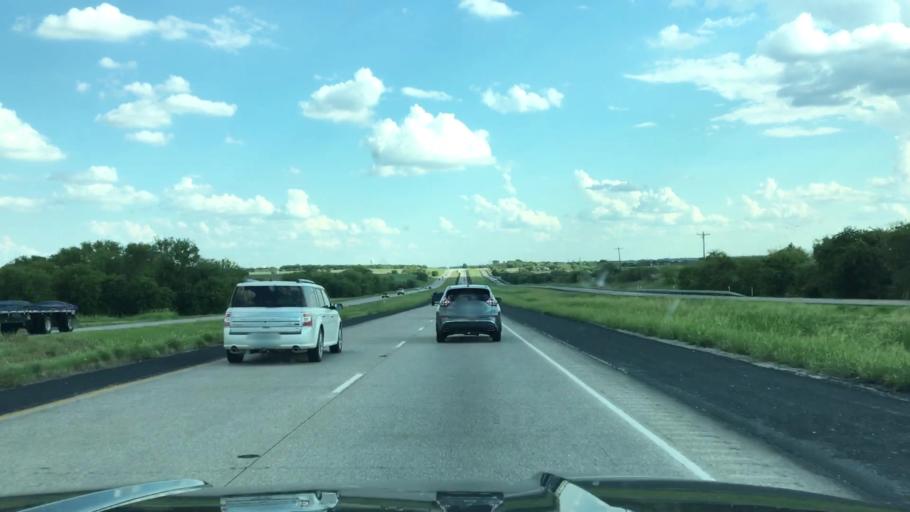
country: US
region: Texas
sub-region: Wise County
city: Newark
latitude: 33.0053
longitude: -97.4362
